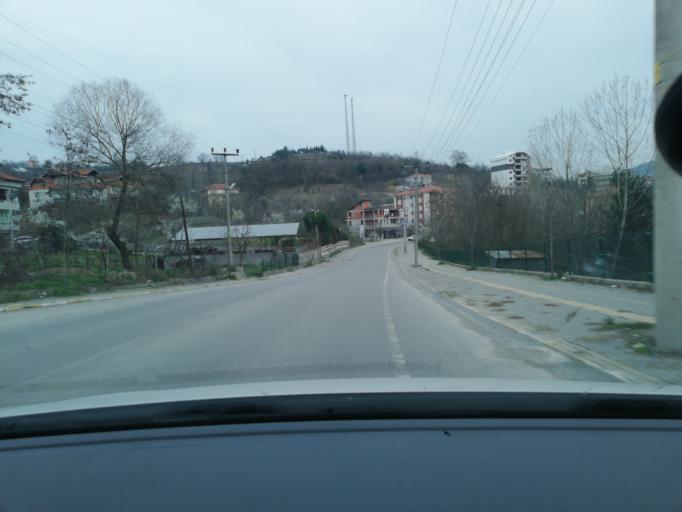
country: TR
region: Zonguldak
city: Gokcebey
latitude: 41.3095
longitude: 32.1297
